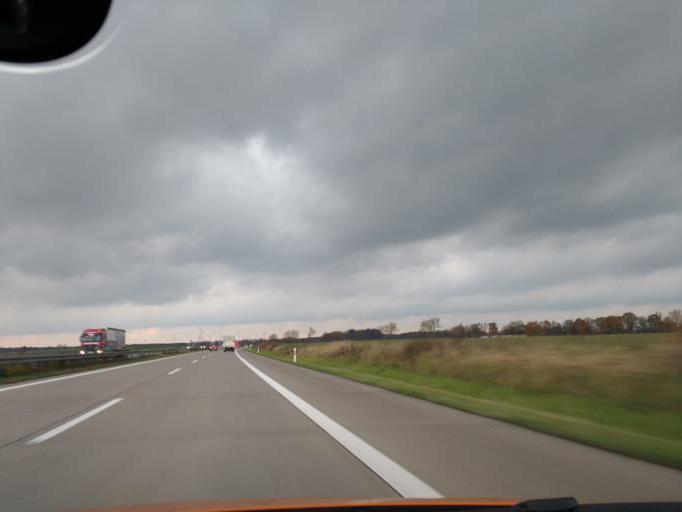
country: DE
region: Brandenburg
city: Heiligengrabe
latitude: 53.1856
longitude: 12.2904
